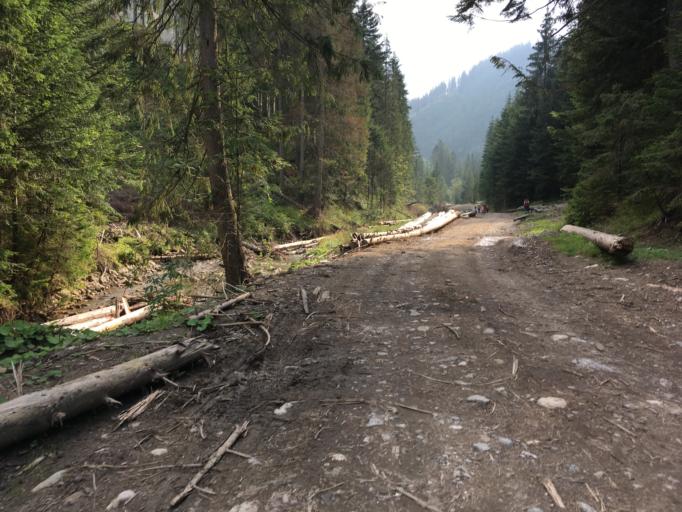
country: PL
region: Lesser Poland Voivodeship
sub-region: Powiat tatrzanski
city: Koscielisko
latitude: 49.2740
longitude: 19.8472
